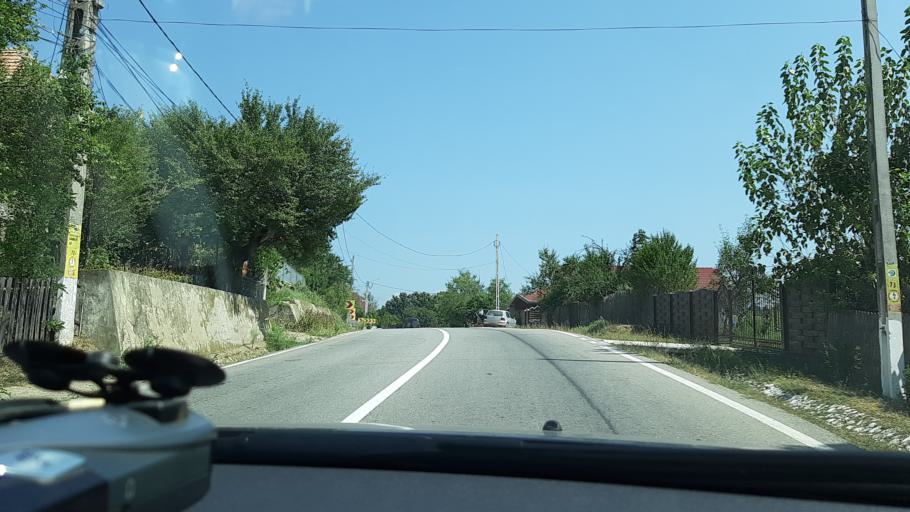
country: RO
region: Gorj
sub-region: Comuna Targu Carbunesti
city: Targu Carbunesti
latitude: 44.9501
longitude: 23.5447
